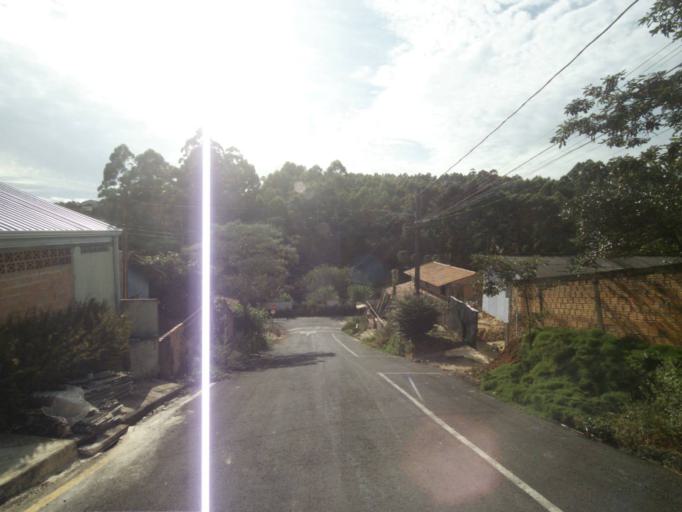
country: BR
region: Parana
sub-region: Telemaco Borba
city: Telemaco Borba
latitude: -24.3477
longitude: -50.6117
